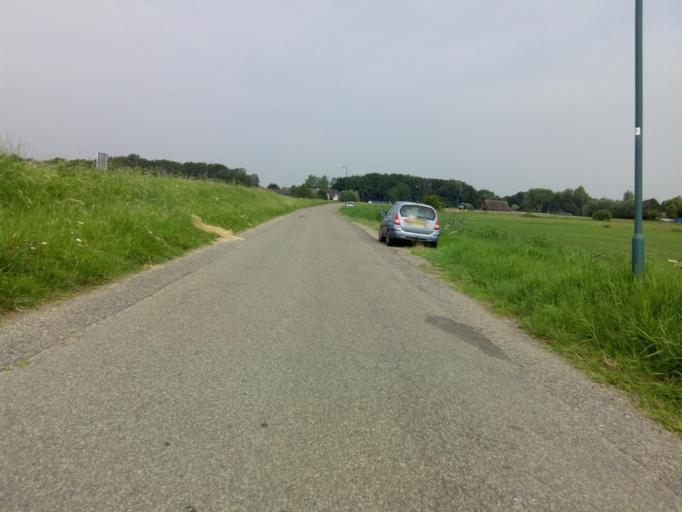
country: NL
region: Utrecht
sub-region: Gemeente Baarn
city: Baarn
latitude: 52.2146
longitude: 5.3105
